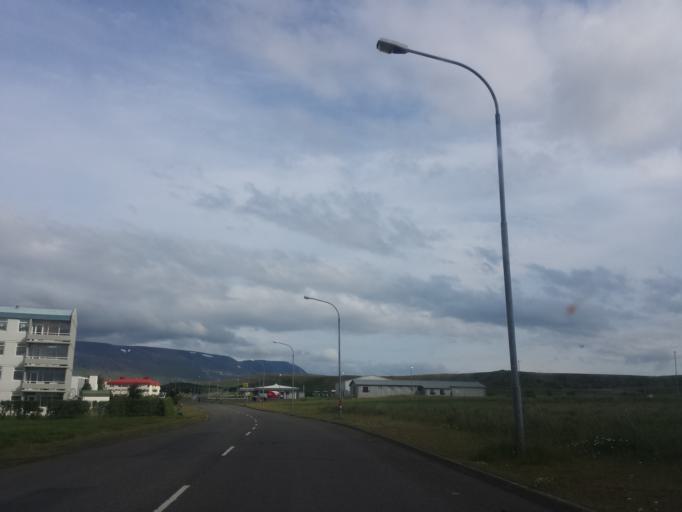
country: IS
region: Northwest
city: Saudarkrokur
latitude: 65.6578
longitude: -20.2902
